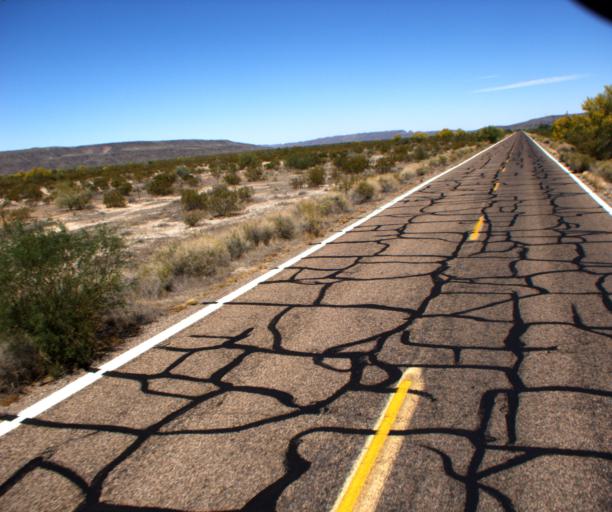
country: US
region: Arizona
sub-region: Pima County
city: Ajo
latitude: 32.4350
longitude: -112.8712
